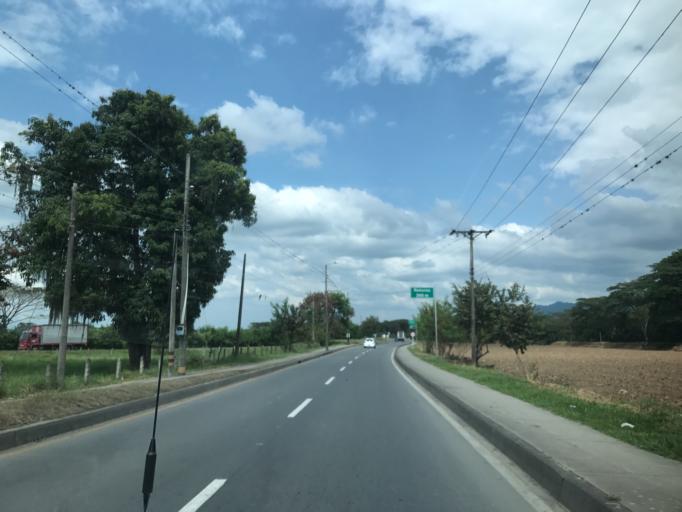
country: CO
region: Valle del Cauca
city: Obando
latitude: 4.5804
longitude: -75.9725
